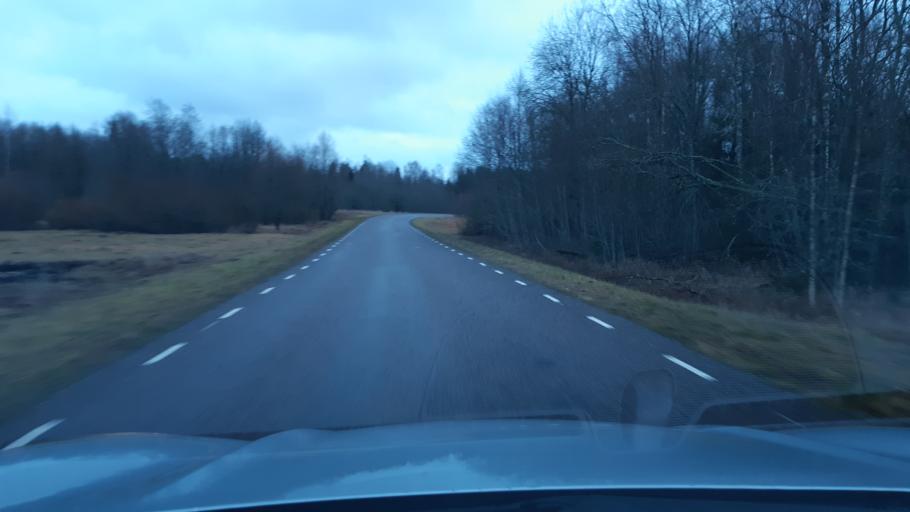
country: EE
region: Raplamaa
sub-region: Rapla vald
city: Rapla
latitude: 58.9859
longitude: 24.7317
